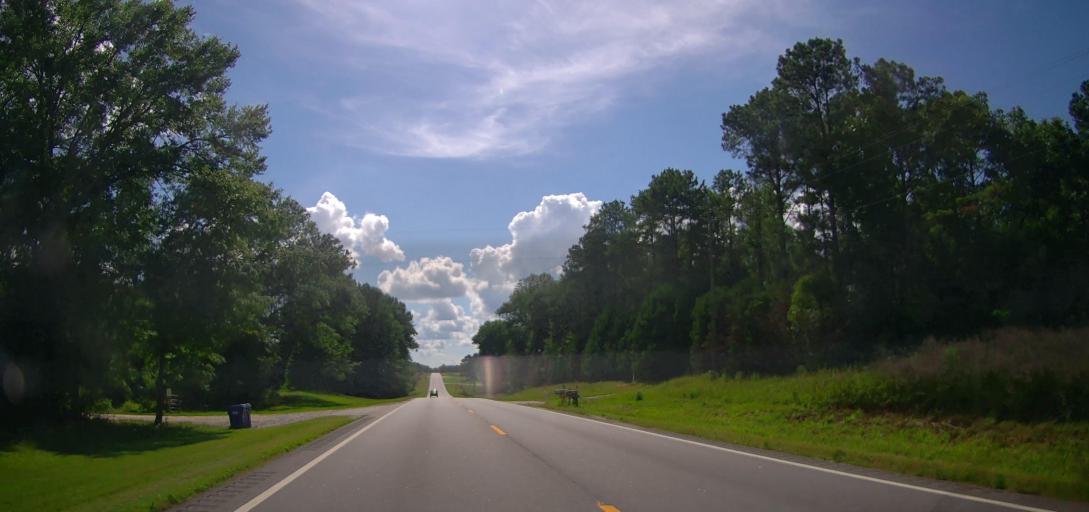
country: US
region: Alabama
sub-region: Lee County
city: Auburn
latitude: 32.4359
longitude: -85.4007
